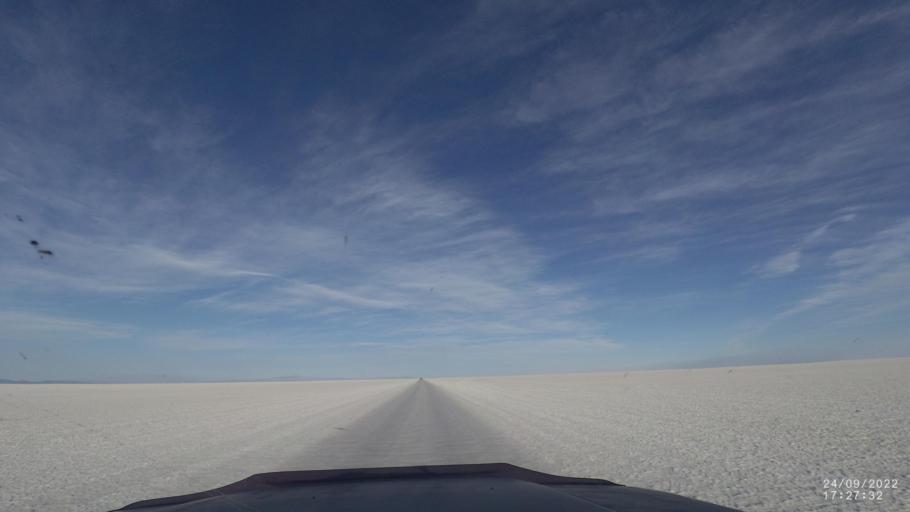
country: BO
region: Potosi
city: Colchani
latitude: -20.3001
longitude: -67.4466
